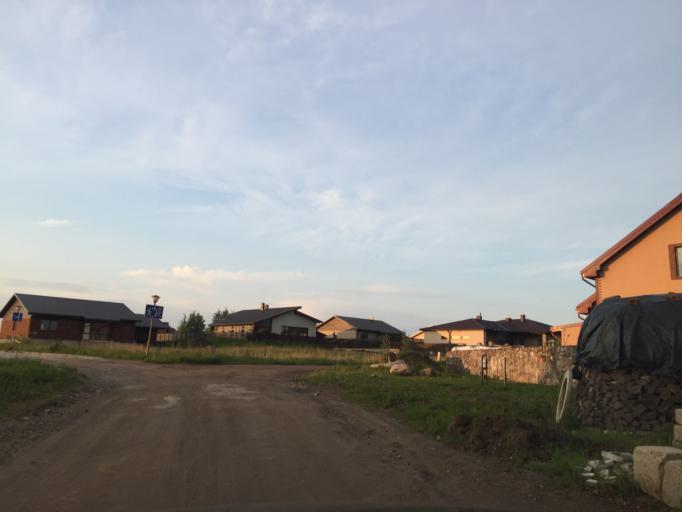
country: LT
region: Klaipedos apskritis
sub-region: Klaipeda
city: Klaipeda
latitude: 55.7567
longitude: 21.1545
